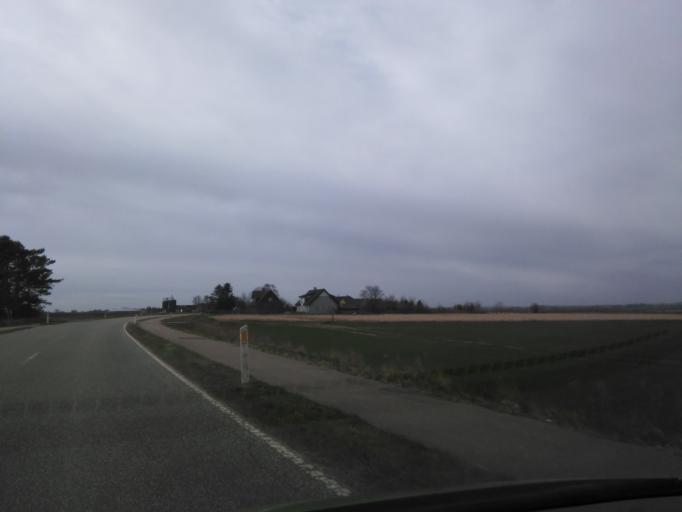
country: DK
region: Central Jutland
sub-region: Arhus Kommune
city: Beder
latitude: 56.0163
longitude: 10.2618
